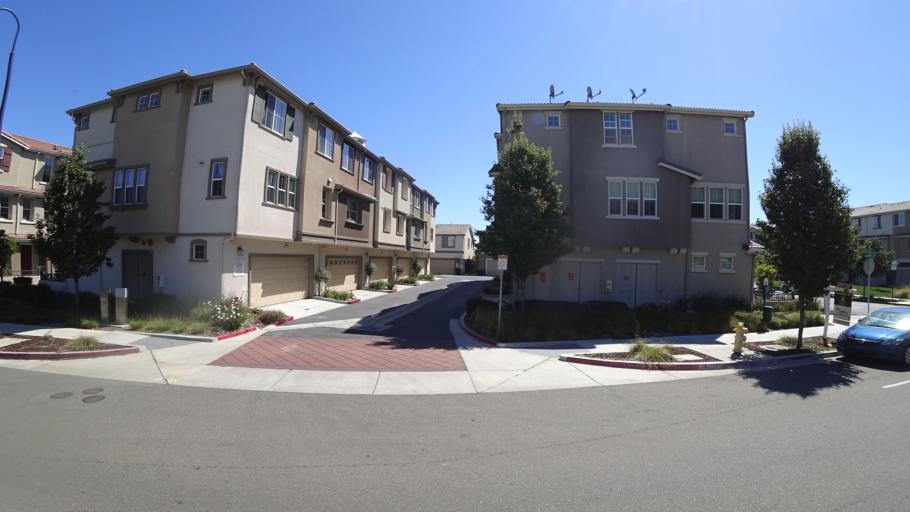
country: US
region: California
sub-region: Alameda County
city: Hayward
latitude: 37.6621
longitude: -122.0947
